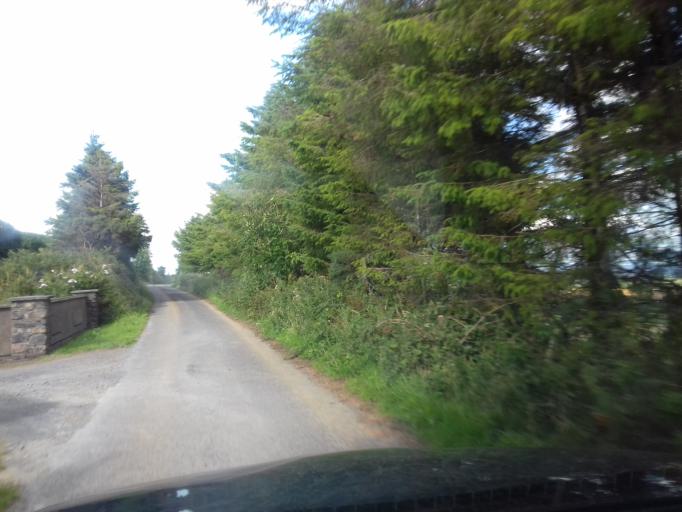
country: IE
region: Leinster
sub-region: Kilkenny
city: Graiguenamanagh
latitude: 52.5521
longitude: -7.0205
